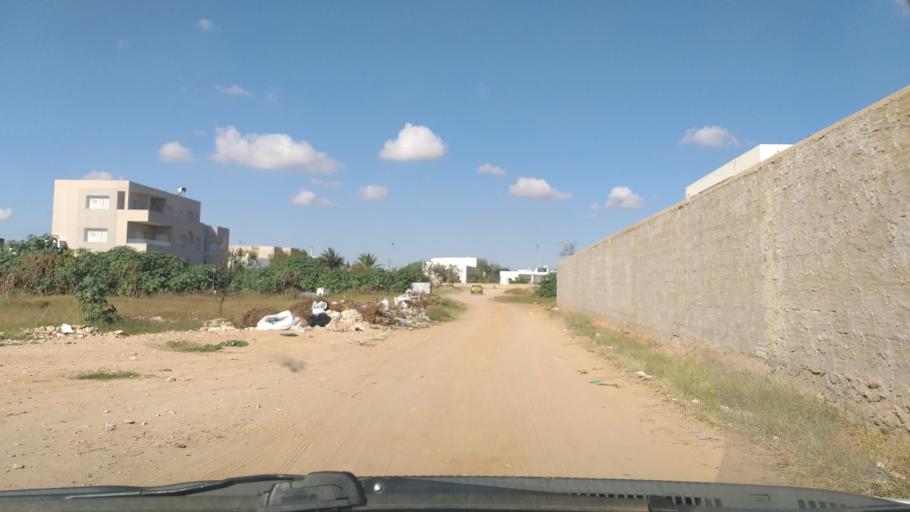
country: TN
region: Safaqis
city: Al Qarmadah
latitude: 34.8019
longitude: 10.7686
